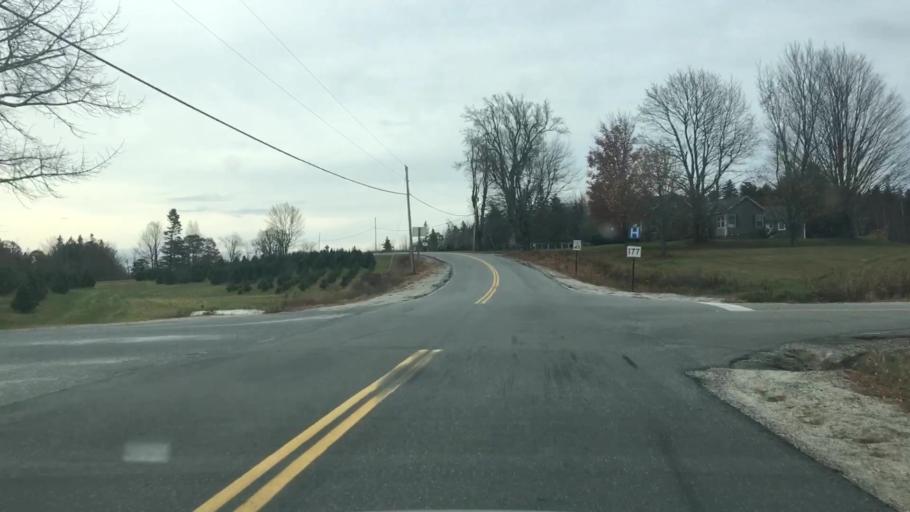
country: US
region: Maine
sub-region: Hancock County
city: Penobscot
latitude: 44.4431
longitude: -68.6365
